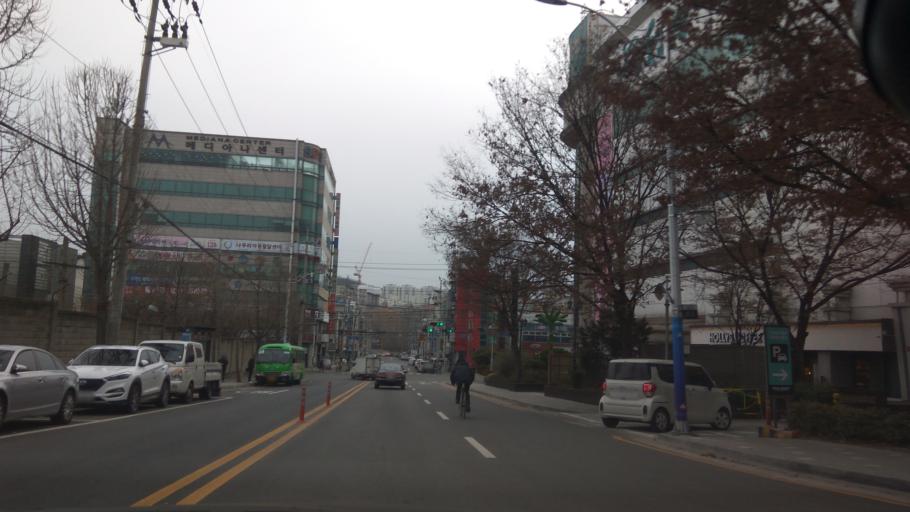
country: KR
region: Incheon
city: Incheon
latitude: 37.4912
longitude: 126.7109
